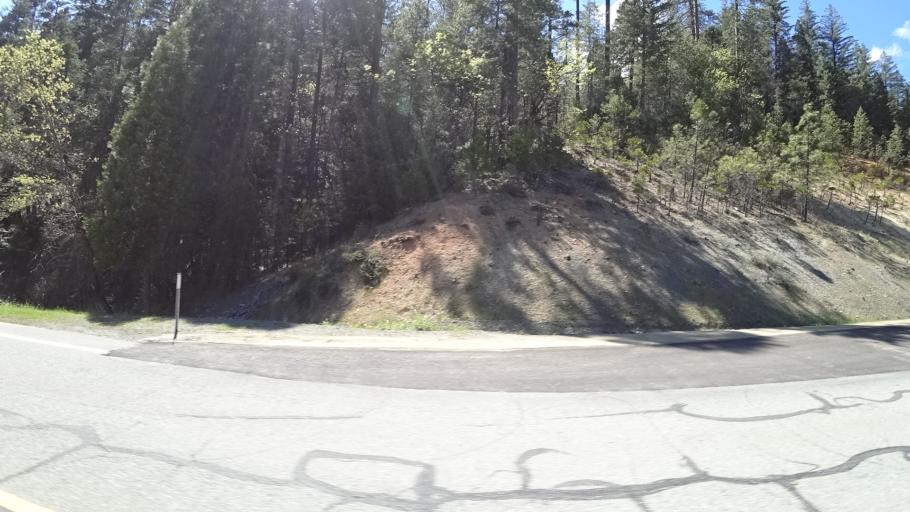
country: US
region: California
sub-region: Trinity County
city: Lewiston
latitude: 40.8711
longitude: -122.8028
